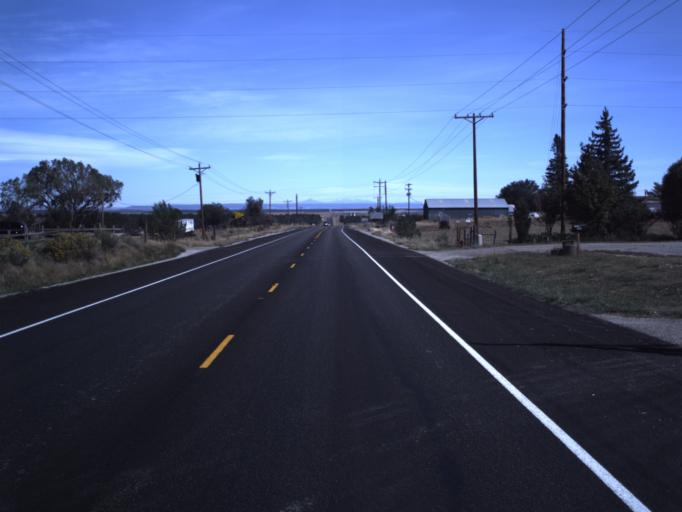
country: US
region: Utah
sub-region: San Juan County
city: Monticello
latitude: 37.8728
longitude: -109.3179
